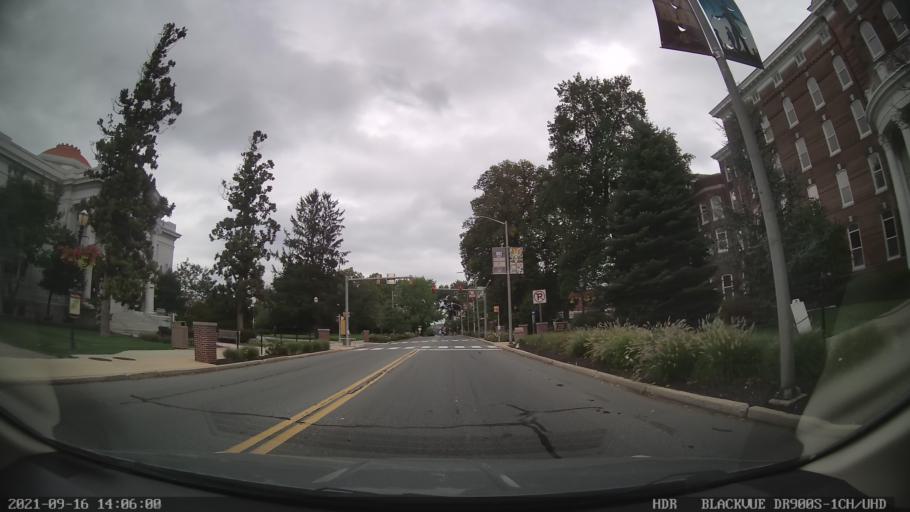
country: US
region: Pennsylvania
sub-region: Berks County
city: Kutztown
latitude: 40.5107
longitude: -75.7833
